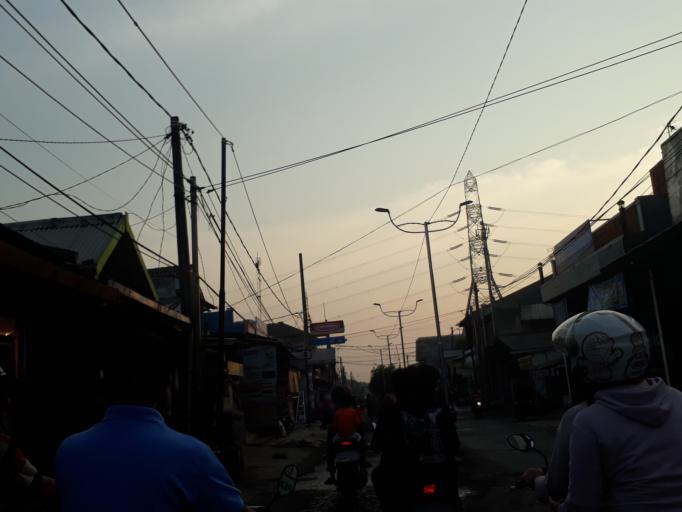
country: ID
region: West Java
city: Bekasi
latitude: -6.2432
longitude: 107.0503
